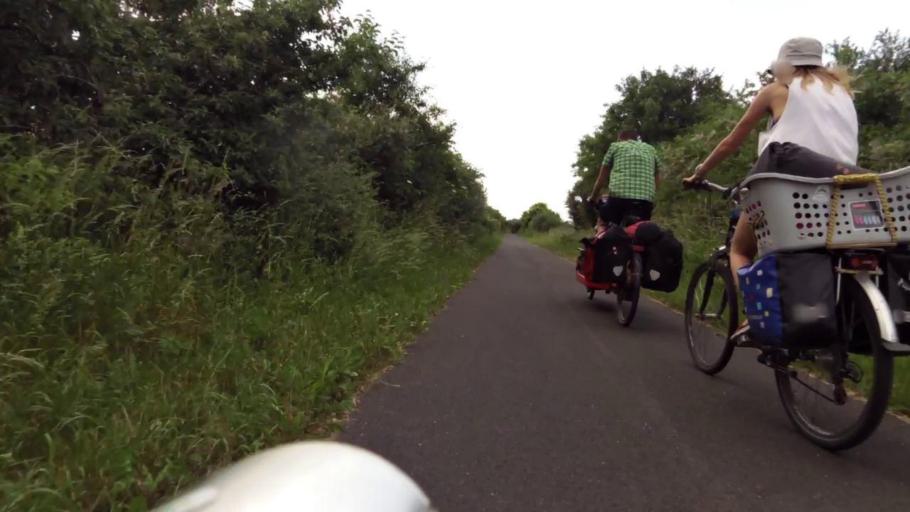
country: PL
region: Kujawsko-Pomorskie
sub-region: Powiat torunski
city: Lubianka
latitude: 53.1171
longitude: 18.4700
